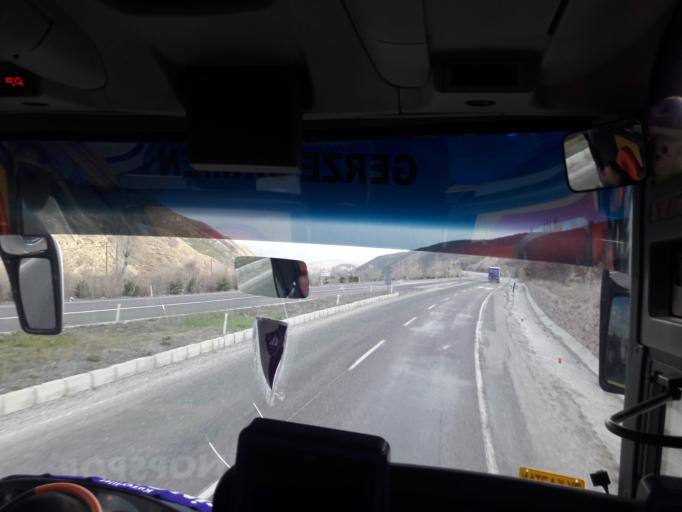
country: TR
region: Cankiri
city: Korgun
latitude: 40.7637
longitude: 33.5284
